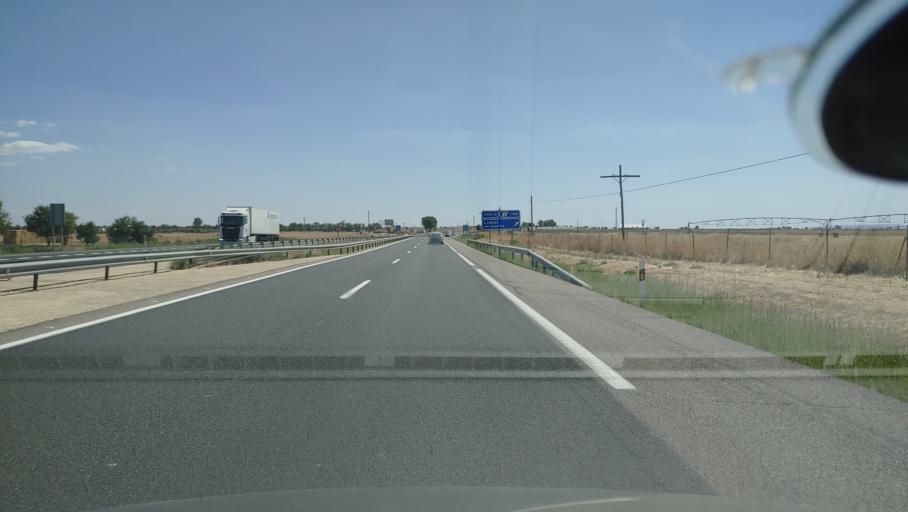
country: ES
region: Castille-La Mancha
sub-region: Provincia de Ciudad Real
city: Villarta de San Juan
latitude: 39.1315
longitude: -3.3798
